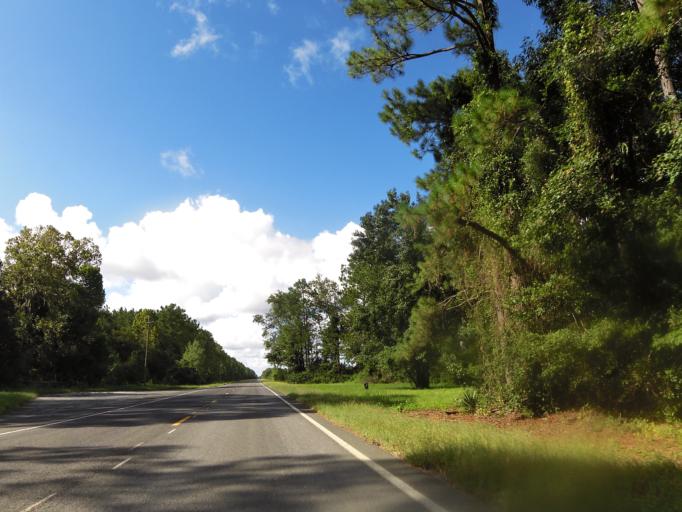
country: US
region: Georgia
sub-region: Camden County
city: Kingsland
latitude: 30.8744
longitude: -81.7051
